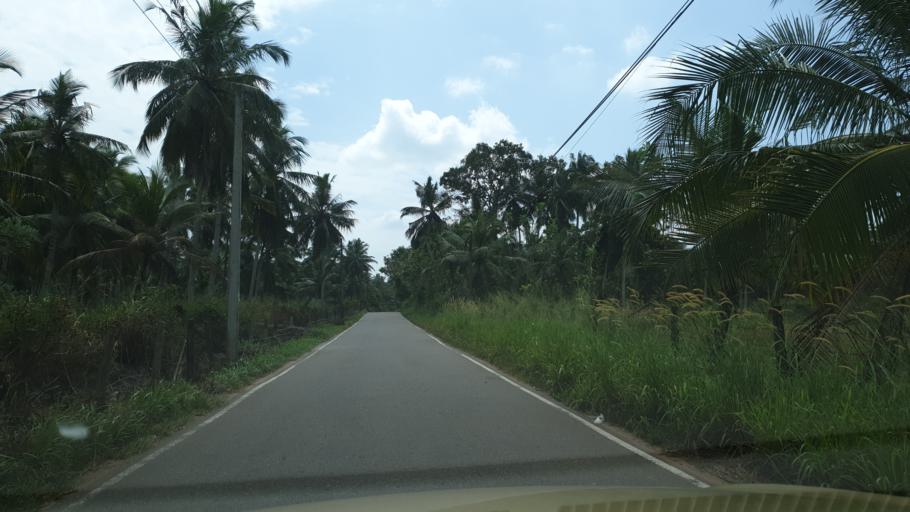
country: LK
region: North Western
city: Kuliyapitiya
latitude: 7.3575
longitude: 79.9676
